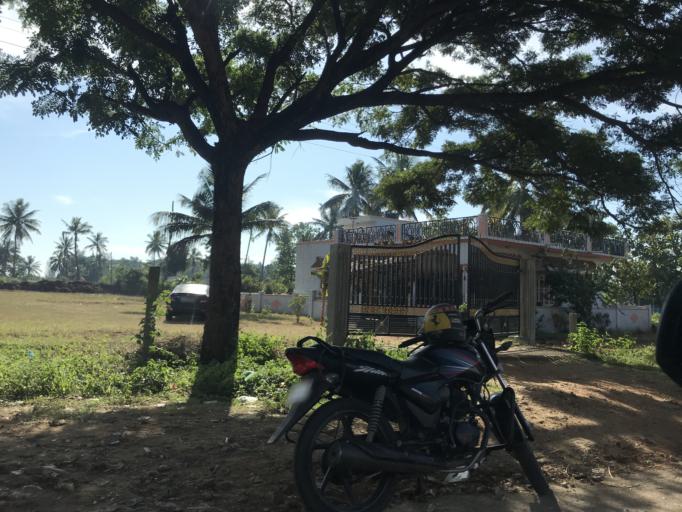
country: IN
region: Karnataka
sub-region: Mysore
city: Mysore
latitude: 12.2520
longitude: 76.6190
